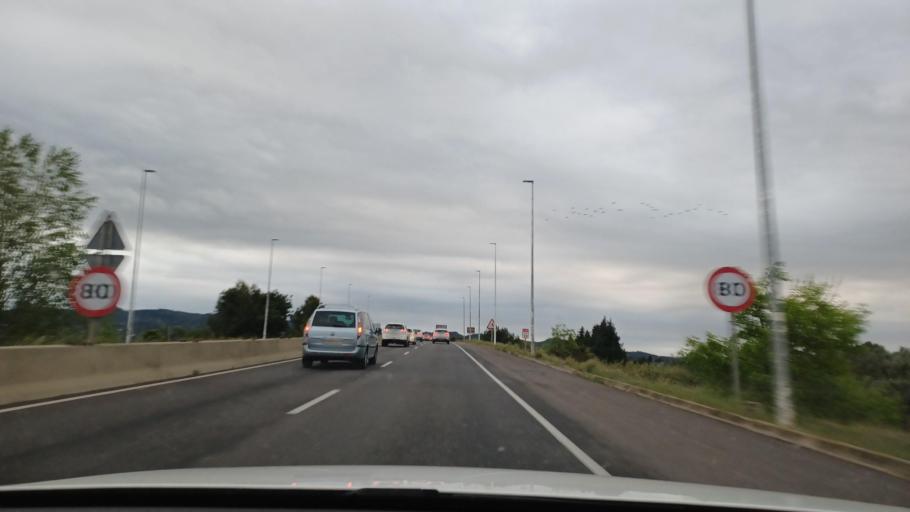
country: ES
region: Catalonia
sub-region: Provincia de Tarragona
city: Tortosa
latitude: 40.8050
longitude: 0.5082
